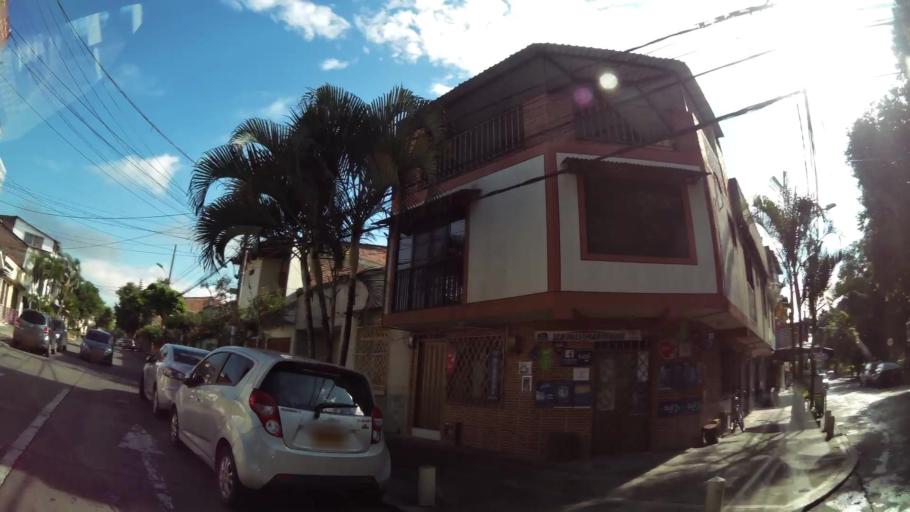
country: CO
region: Valle del Cauca
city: Cali
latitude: 3.4321
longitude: -76.5294
